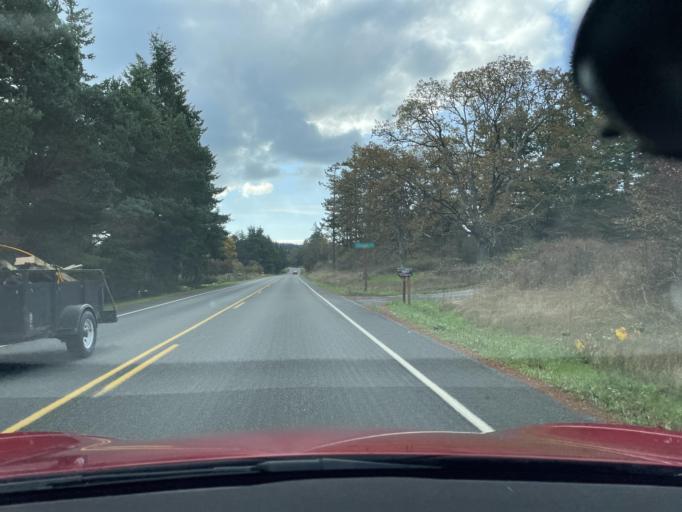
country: US
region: Washington
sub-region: San Juan County
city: Friday Harbor
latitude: 48.5077
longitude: -123.0363
